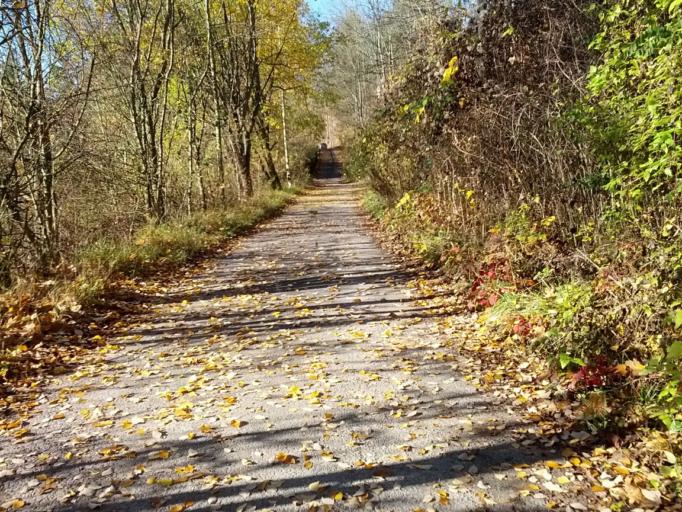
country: DE
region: Thuringia
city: Thal
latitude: 50.9611
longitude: 10.3974
